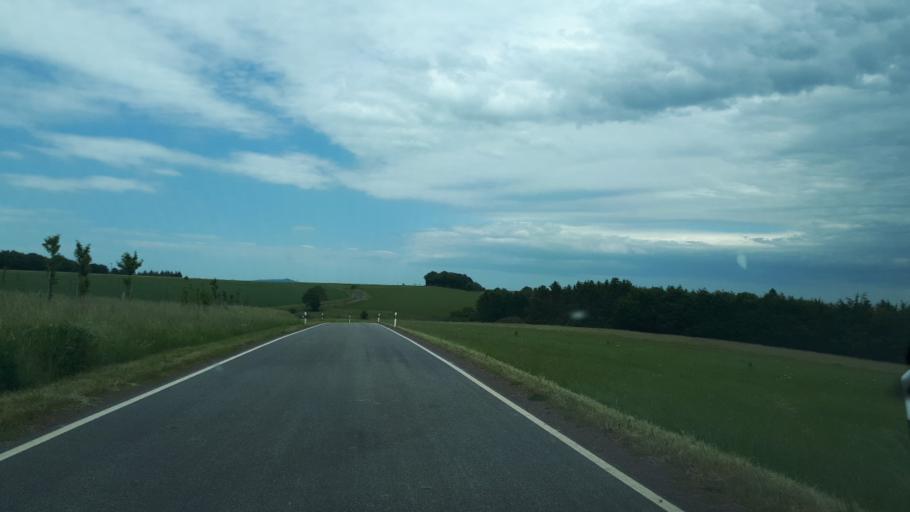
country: DE
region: Rheinland-Pfalz
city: Immerath
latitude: 50.1302
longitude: 6.9498
